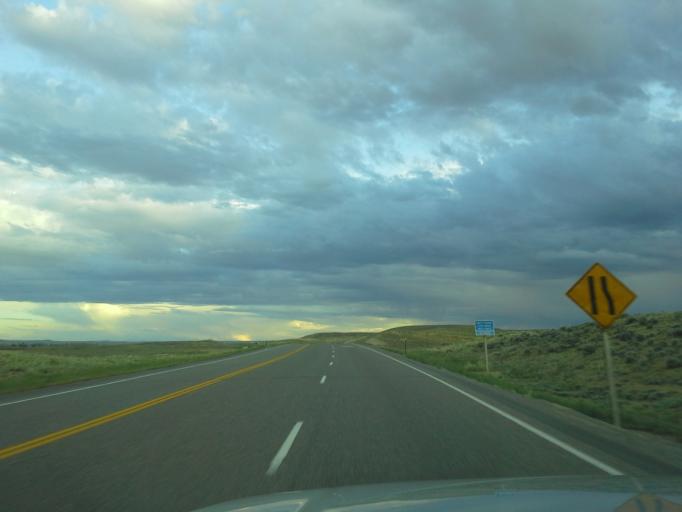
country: US
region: Wyoming
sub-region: Big Horn County
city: Basin
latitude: 44.3437
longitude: -108.0488
